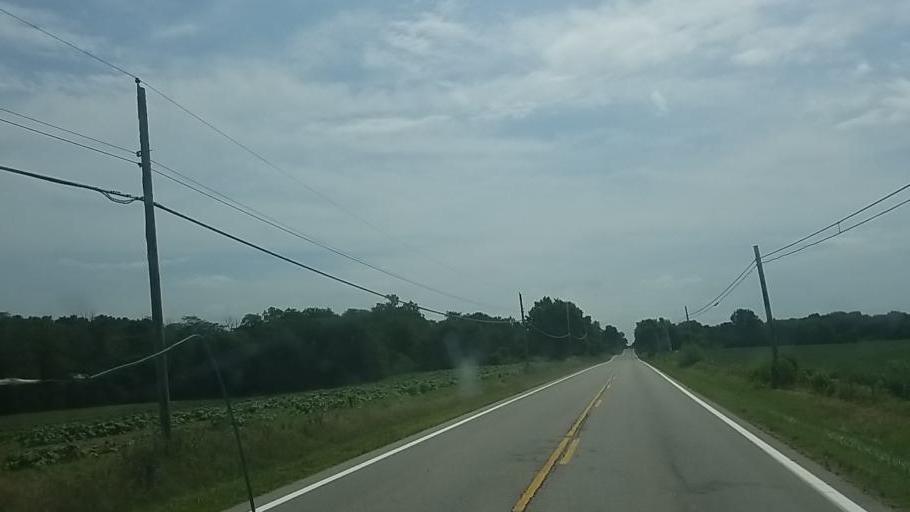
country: US
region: Ohio
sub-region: Delaware County
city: Sunbury
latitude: 40.2327
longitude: -82.8344
